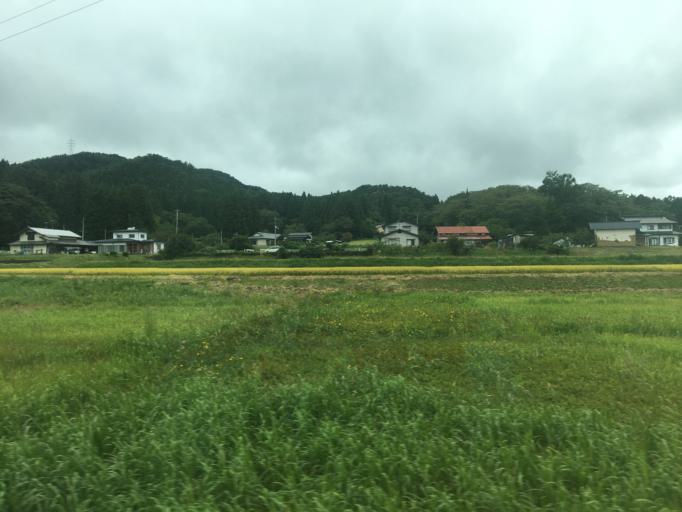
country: JP
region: Iwate
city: Shizukuishi
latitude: 39.7048
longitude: 141.0593
